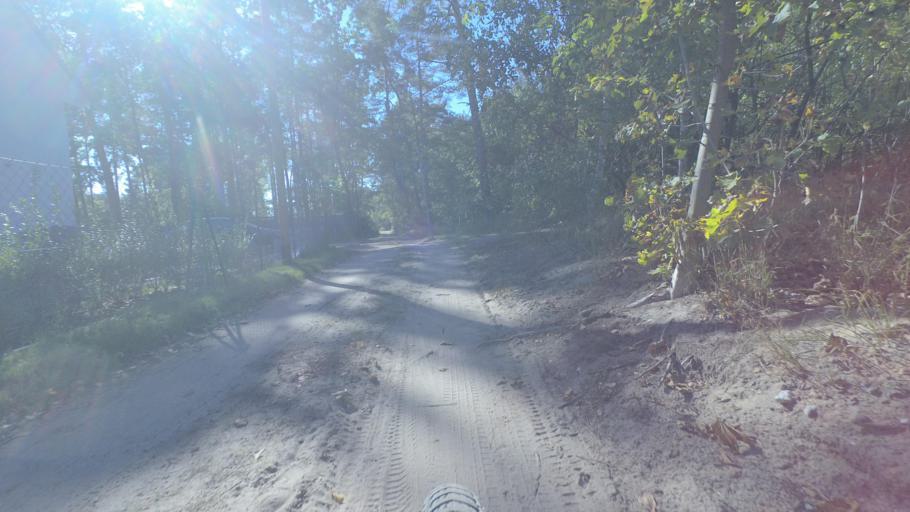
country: DE
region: Brandenburg
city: Am Mellensee
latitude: 52.1721
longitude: 13.3927
